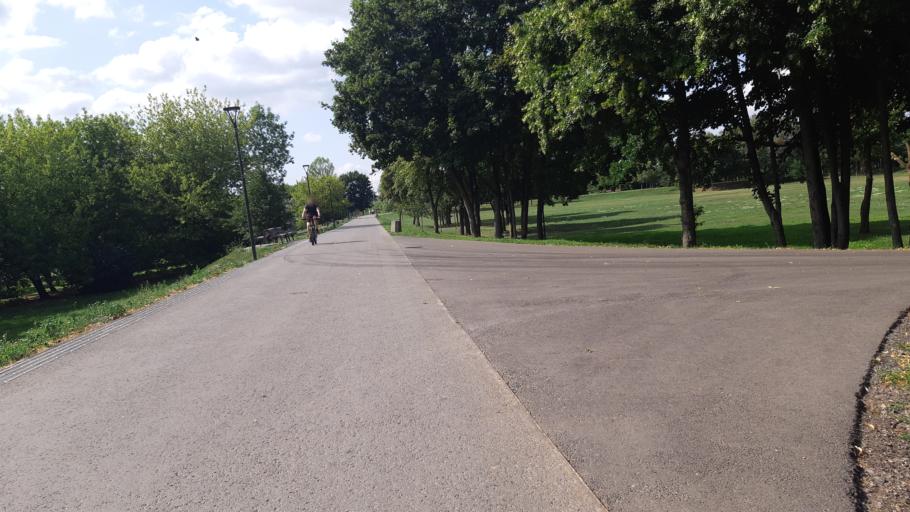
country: LT
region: Kauno apskritis
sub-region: Kaunas
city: Kaunas
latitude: 54.8968
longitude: 23.8800
